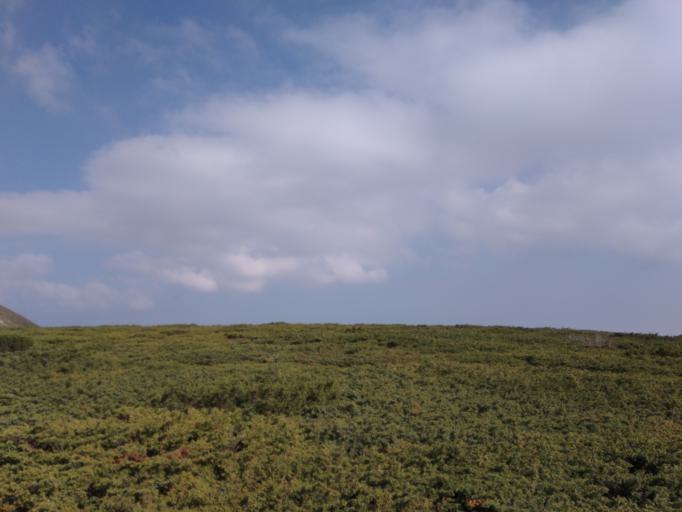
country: BG
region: Plovdiv
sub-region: Obshtina Karlovo
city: Kalofer
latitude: 42.7359
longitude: 24.9839
